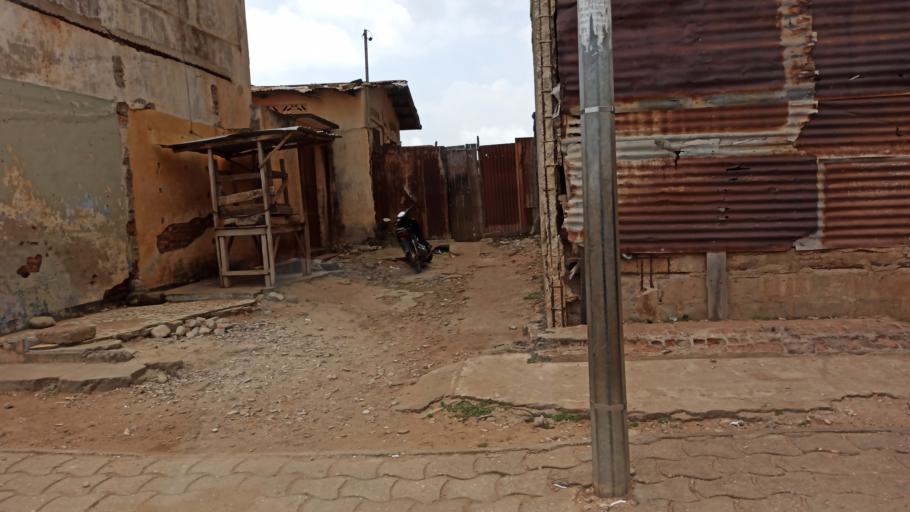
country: BJ
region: Queme
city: Porto-Novo
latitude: 6.4704
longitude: 2.6258
